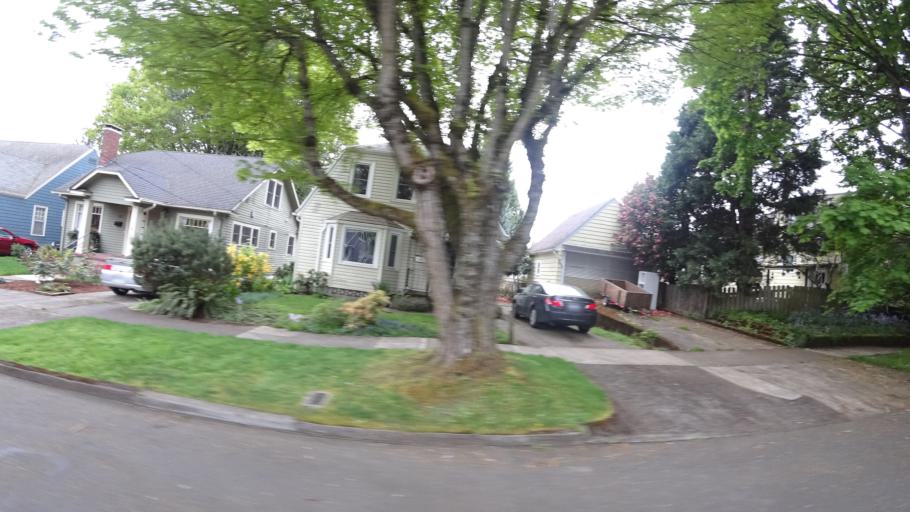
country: US
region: Oregon
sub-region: Clackamas County
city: Milwaukie
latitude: 45.4701
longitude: -122.6525
